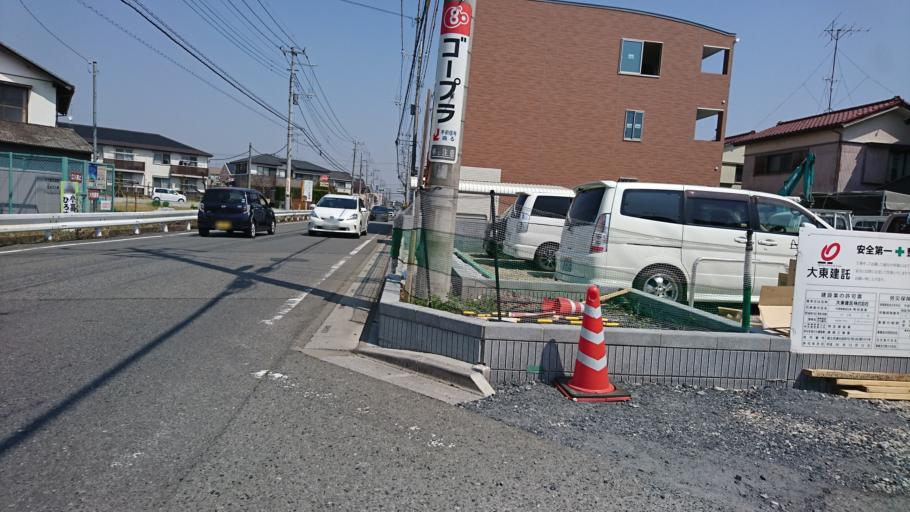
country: JP
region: Saitama
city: Kawagoe
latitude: 35.9337
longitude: 139.4755
